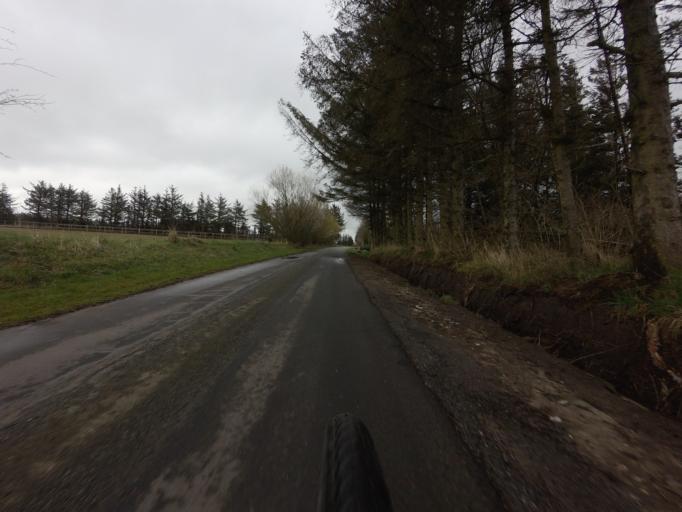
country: DK
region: North Denmark
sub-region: Jammerbugt Kommune
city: Pandrup
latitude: 57.3225
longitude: 9.7930
